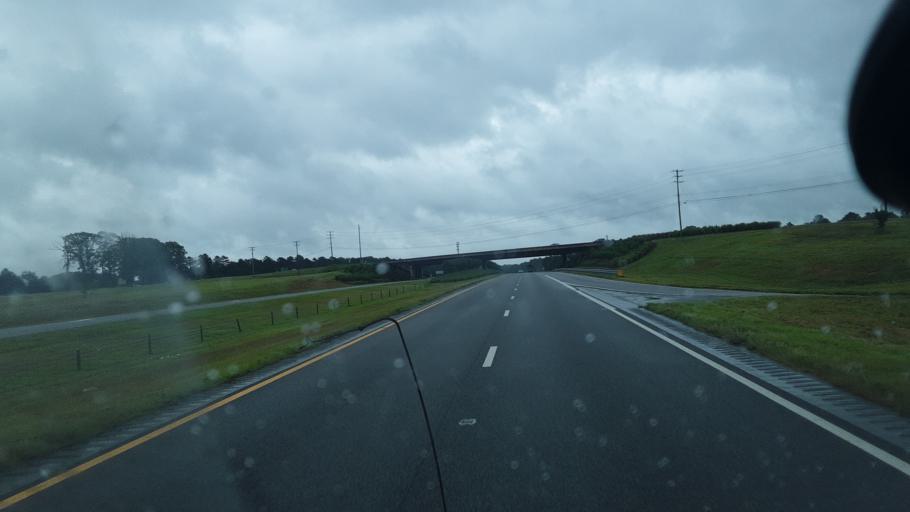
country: US
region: North Carolina
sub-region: Davidson County
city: Wallburg
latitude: 36.0485
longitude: -80.1276
